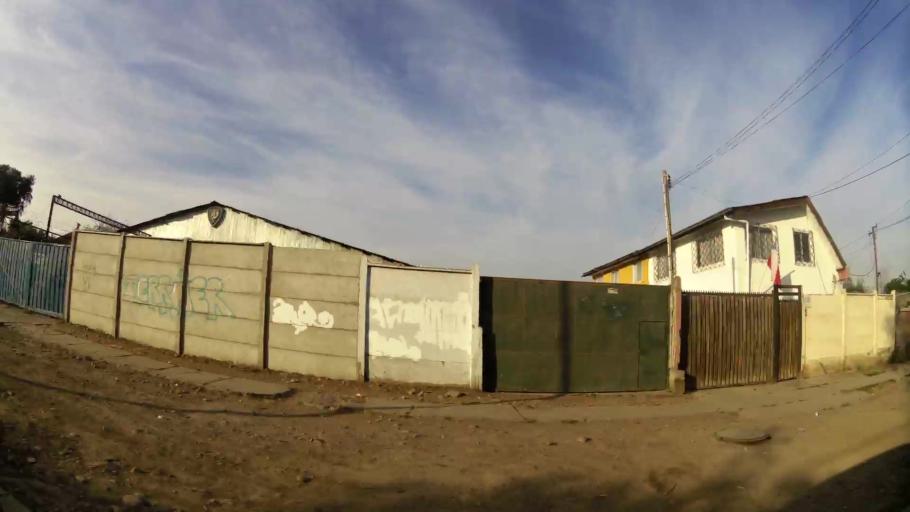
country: CL
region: Santiago Metropolitan
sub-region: Provincia de Santiago
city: La Pintana
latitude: -33.5296
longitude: -70.6744
